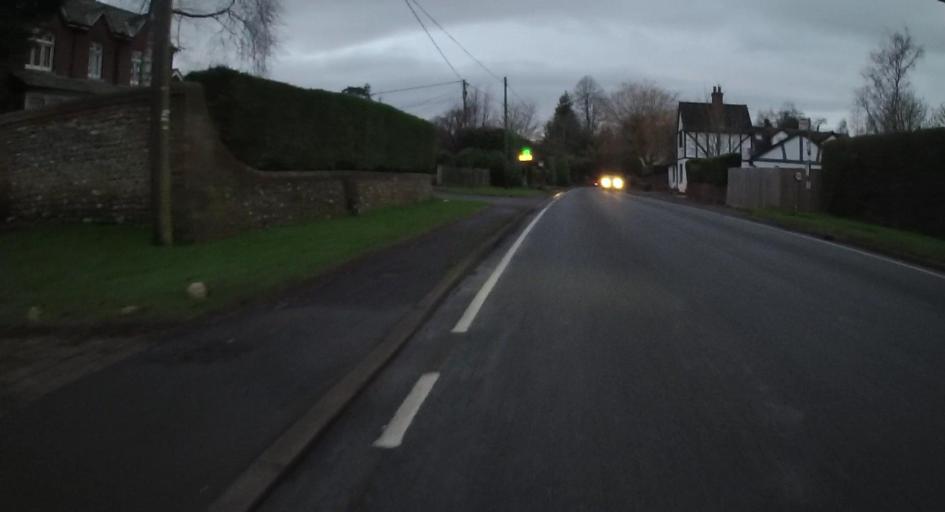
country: GB
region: England
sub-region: Hampshire
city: Four Marks
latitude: 51.0821
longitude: -1.1289
